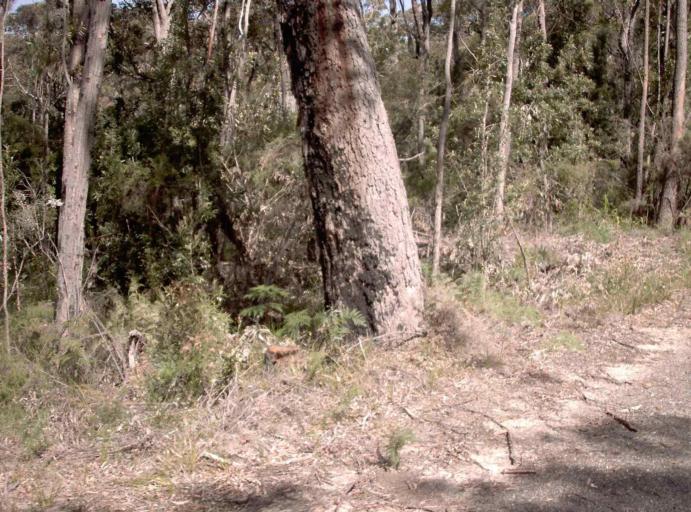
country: AU
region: New South Wales
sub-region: Bega Valley
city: Eden
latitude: -37.5438
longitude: 149.6982
